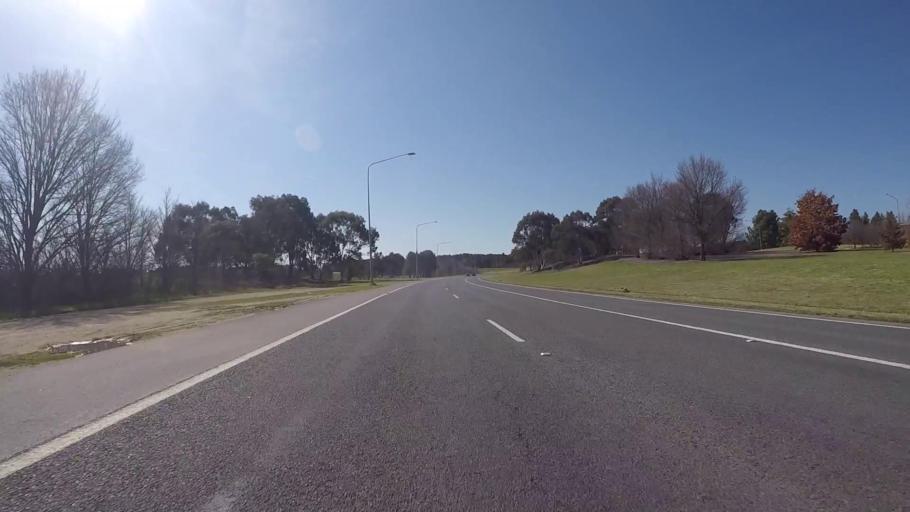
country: AU
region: Australian Capital Territory
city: Forrest
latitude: -35.3186
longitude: 149.0892
